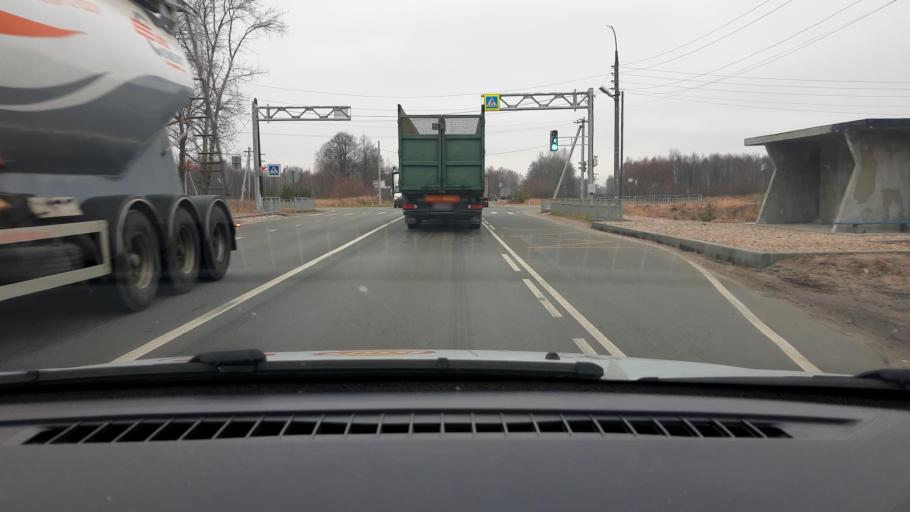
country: RU
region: Nizjnij Novgorod
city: Gorodets
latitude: 56.5678
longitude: 43.4834
